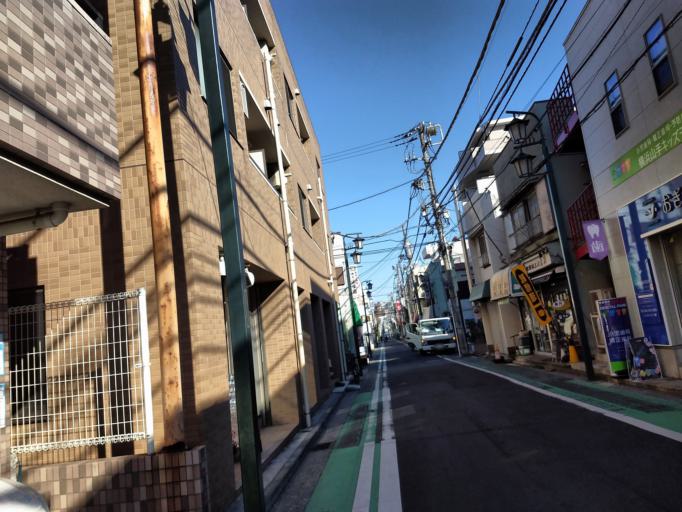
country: JP
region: Kanagawa
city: Yokohama
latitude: 35.4294
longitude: 139.6471
